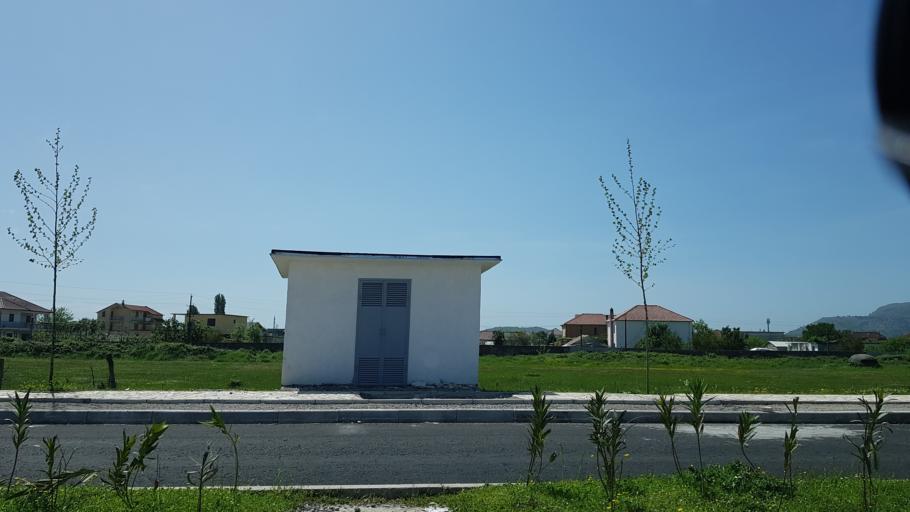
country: AL
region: Shkoder
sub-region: Rrethi i Shkodres
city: Shkoder
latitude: 42.0840
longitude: 19.4996
